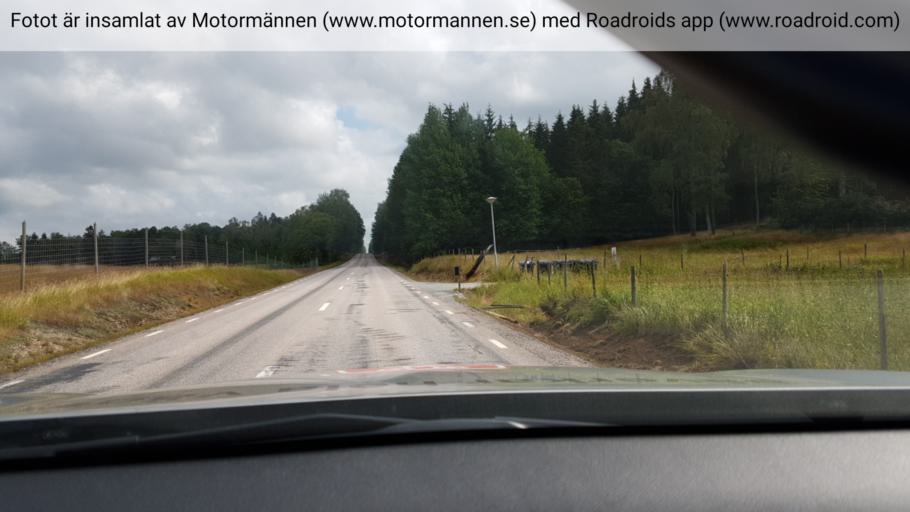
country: SE
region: Vaestra Goetaland
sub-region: Svenljunga Kommun
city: Svenljunga
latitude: 57.4941
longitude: 13.0735
